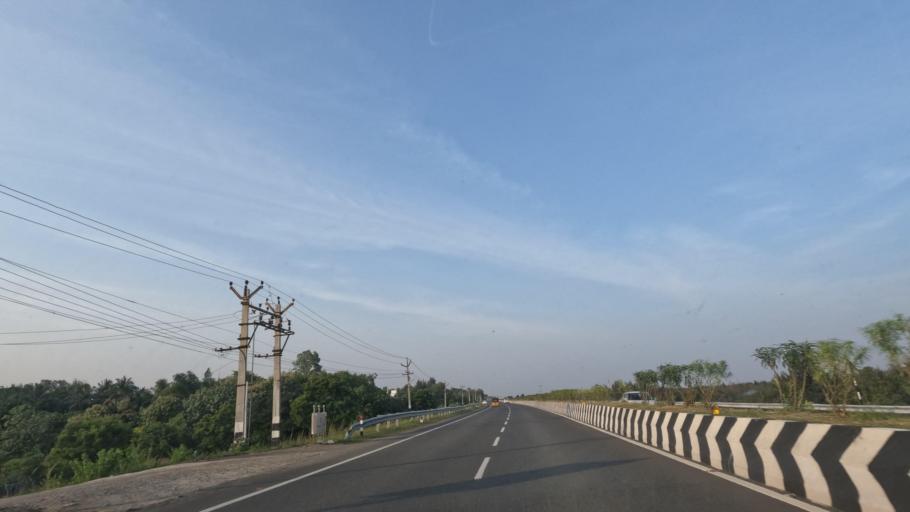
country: IN
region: Tamil Nadu
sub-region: Kancheepuram
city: Mamallapuram
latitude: 12.7107
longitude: 80.2251
